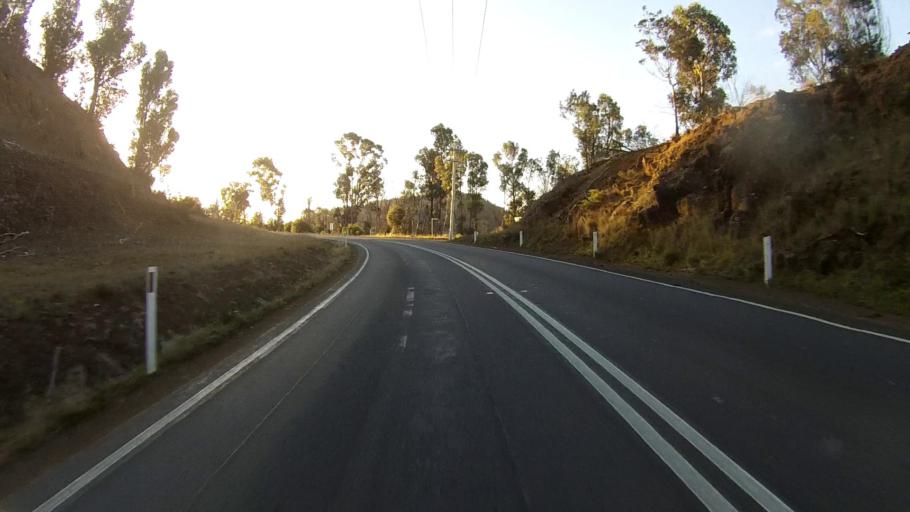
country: AU
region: Tasmania
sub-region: Sorell
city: Sorell
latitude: -42.8530
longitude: 147.8228
